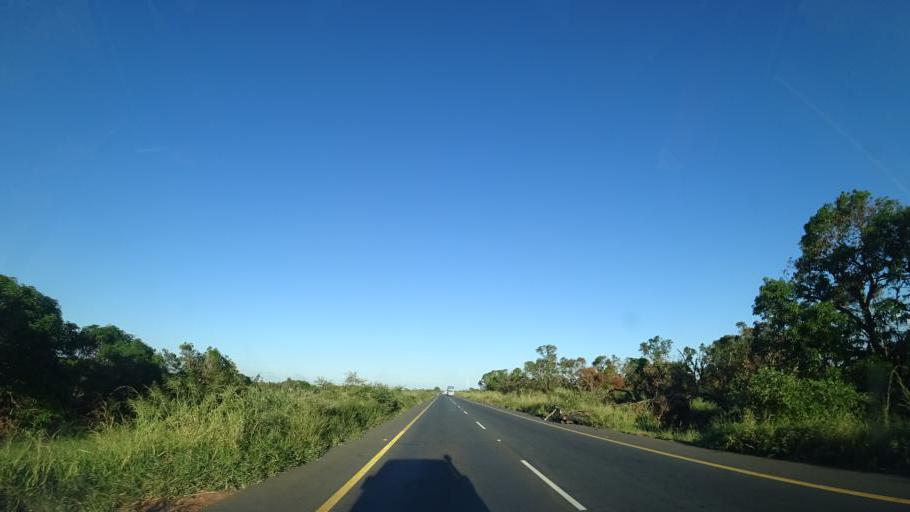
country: MZ
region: Sofala
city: Dondo
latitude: -19.3361
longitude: 34.3283
